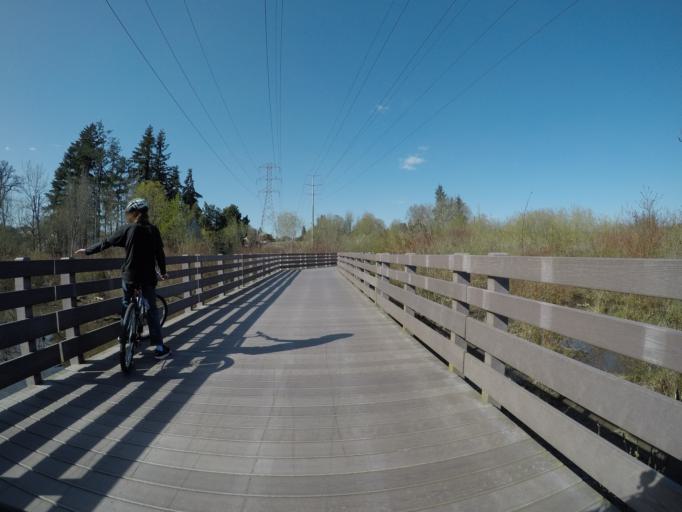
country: US
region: Oregon
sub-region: Washington County
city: Oak Hills
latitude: 45.5416
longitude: -122.8462
